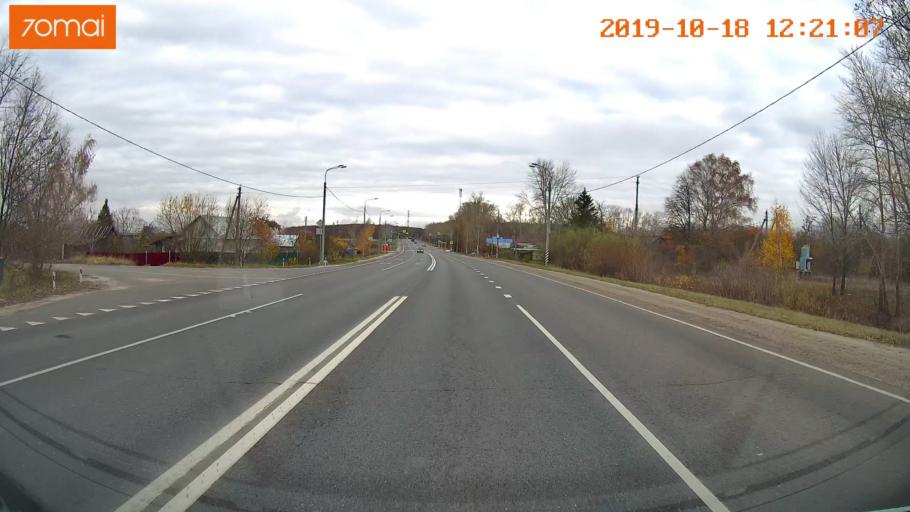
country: RU
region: Rjazan
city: Bagramovo
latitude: 54.5069
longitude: 39.4870
